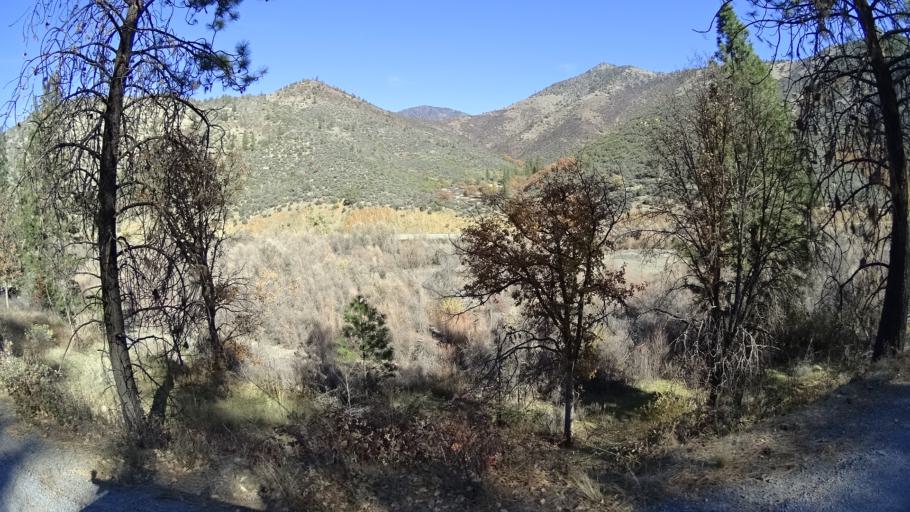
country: US
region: California
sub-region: Siskiyou County
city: Yreka
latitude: 41.8400
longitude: -122.6732
